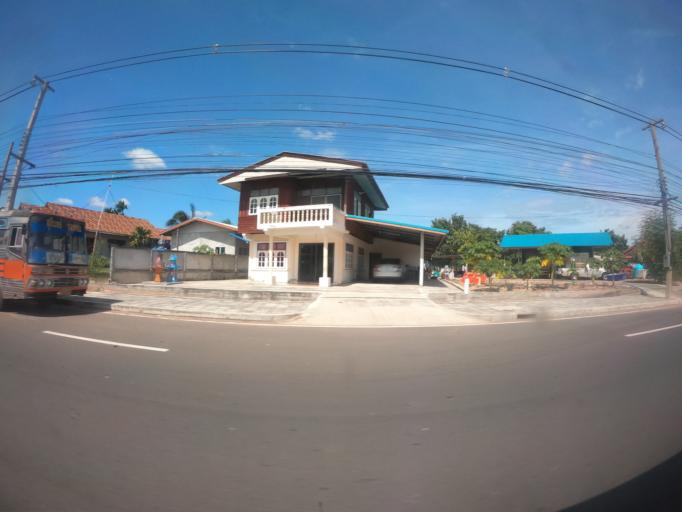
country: TH
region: Surin
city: Prasat
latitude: 14.6185
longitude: 103.4141
